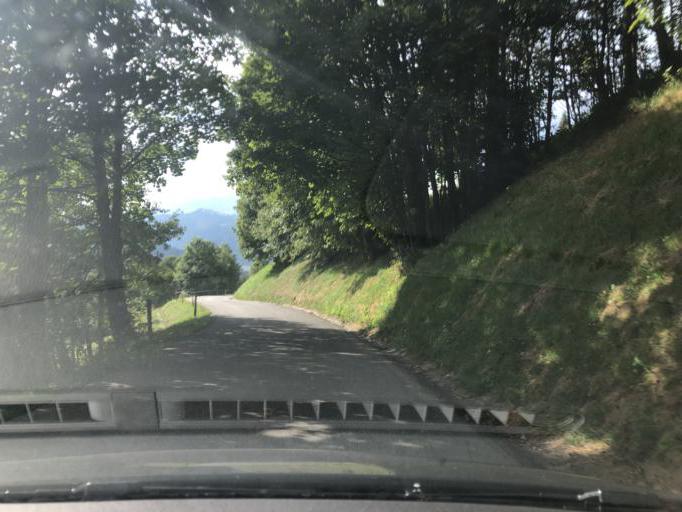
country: FR
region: Rhone-Alpes
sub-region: Departement de la Haute-Savoie
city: Megeve
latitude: 45.8340
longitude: 6.6510
